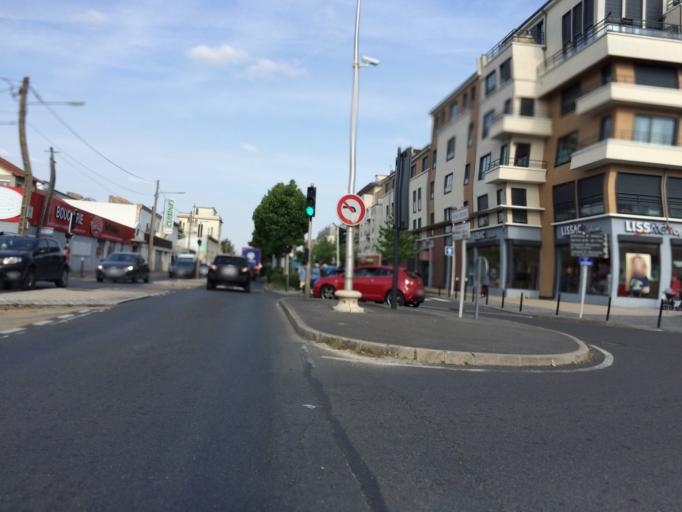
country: FR
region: Ile-de-France
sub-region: Departement de l'Essonne
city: Paray-Vieille-Poste
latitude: 48.7057
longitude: 2.3628
